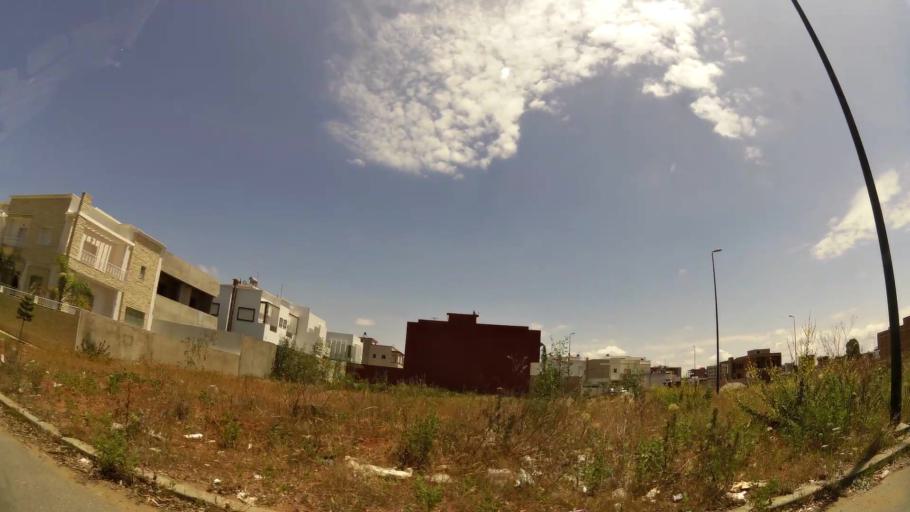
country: MA
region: Gharb-Chrarda-Beni Hssen
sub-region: Kenitra Province
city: Kenitra
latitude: 34.2659
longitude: -6.6313
